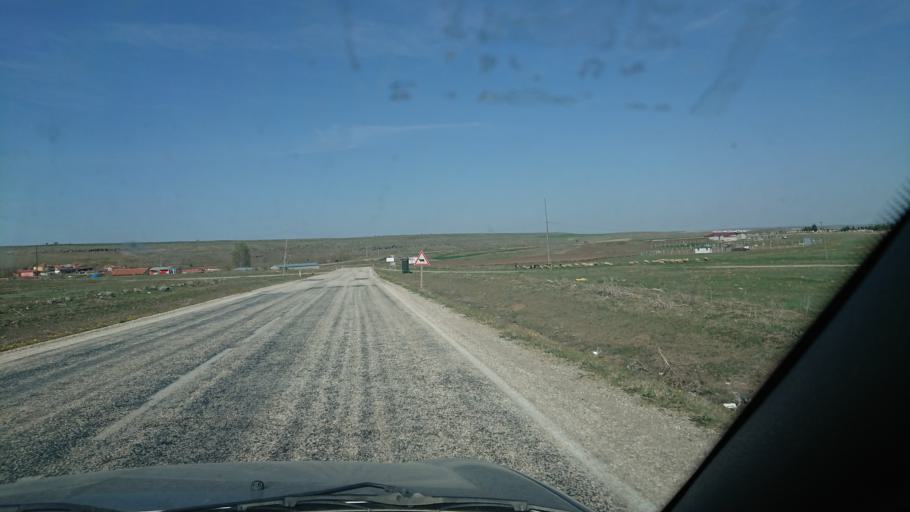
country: TR
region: Eskisehir
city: Eskisehir
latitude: 39.6746
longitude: 30.4818
